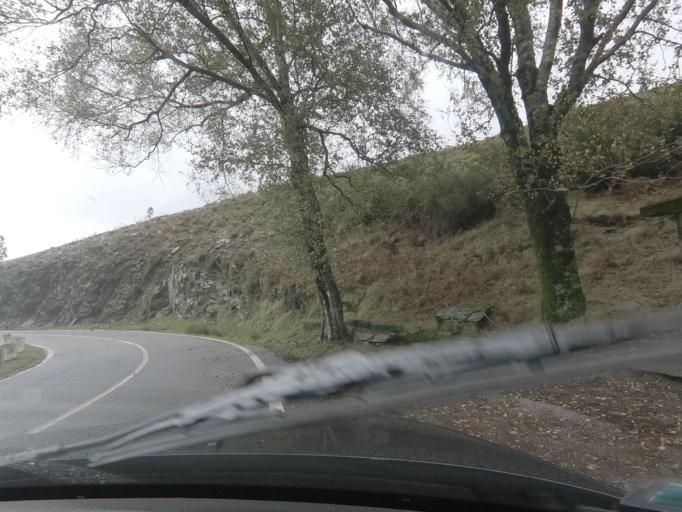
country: PT
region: Vila Real
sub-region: Mondim de Basto
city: Mondim de Basto
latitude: 41.3360
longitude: -7.8633
